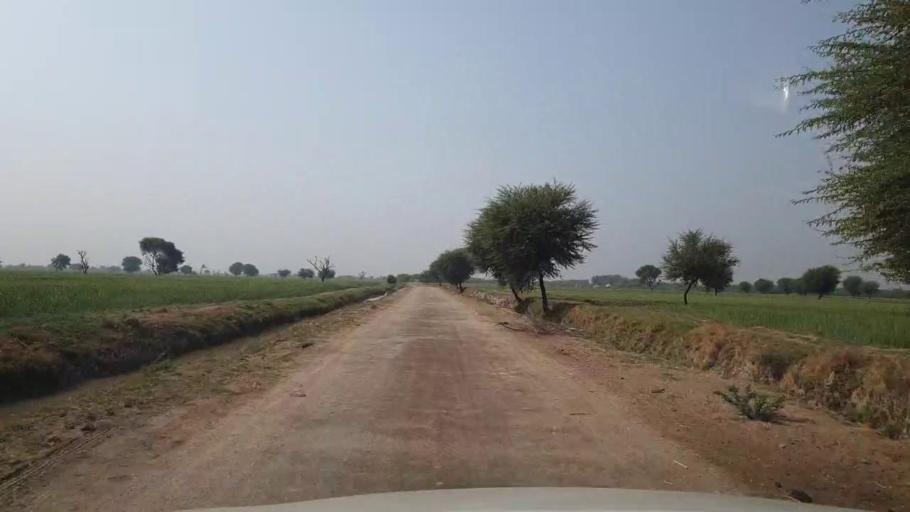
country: PK
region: Sindh
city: Umarkot
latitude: 25.4437
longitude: 69.7063
